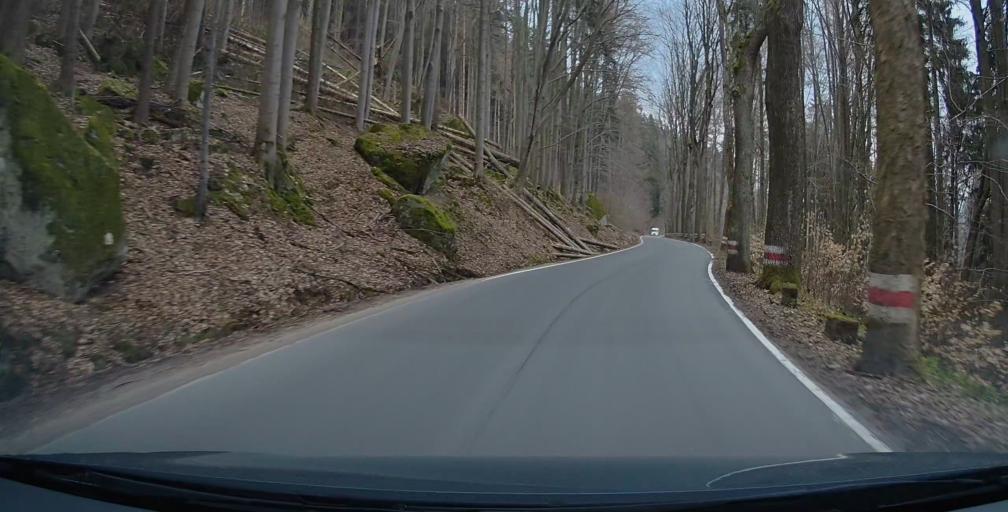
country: PL
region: Lower Silesian Voivodeship
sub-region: Powiat klodzki
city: Radkow
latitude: 50.4852
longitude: 16.3743
